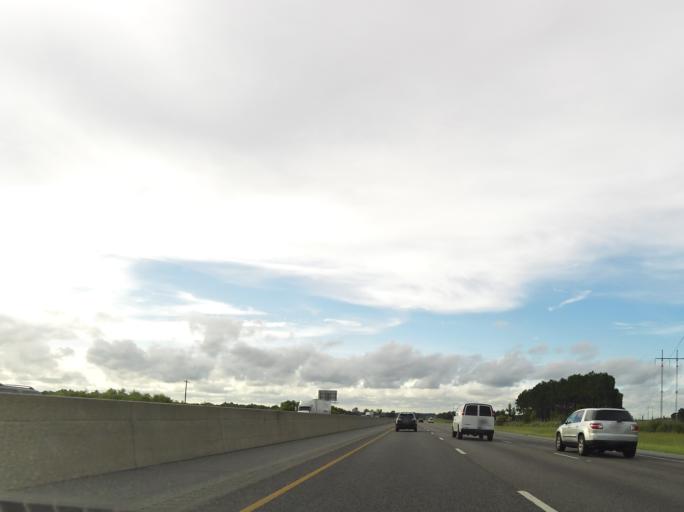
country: US
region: Georgia
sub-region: Tift County
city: Tifton
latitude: 31.5840
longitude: -83.5543
